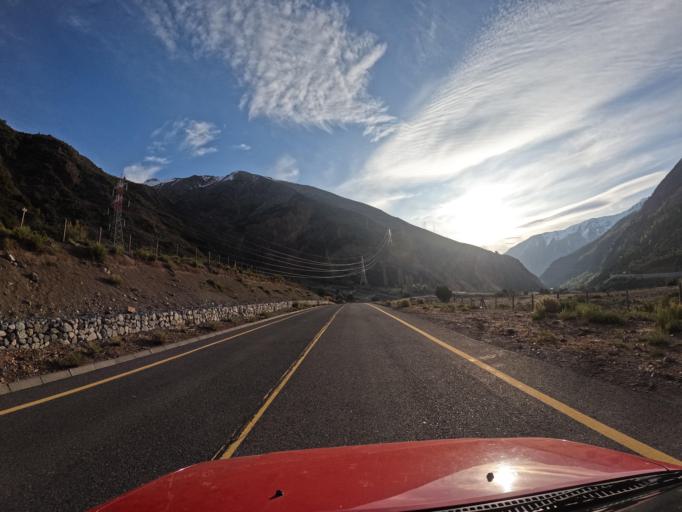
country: CL
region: Maule
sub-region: Provincia de Linares
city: Colbun
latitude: -35.8318
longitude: -70.7309
